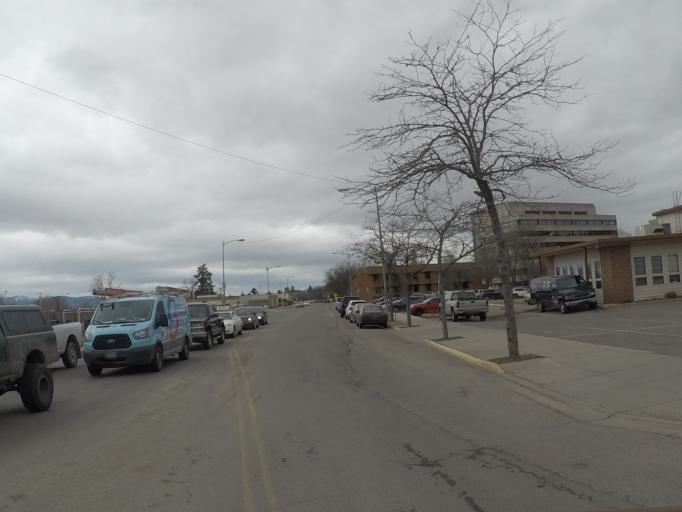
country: US
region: Montana
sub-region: Missoula County
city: Missoula
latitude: 46.8726
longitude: -113.9992
